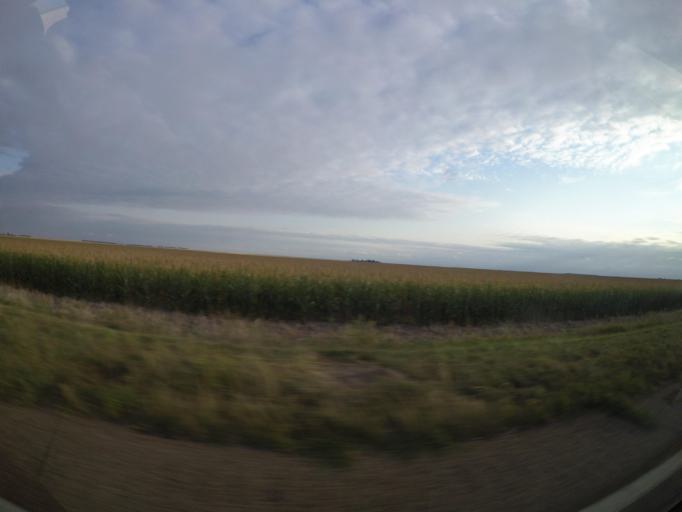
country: US
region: Colorado
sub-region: Yuma County
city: Wray
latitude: 39.7025
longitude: -102.2780
